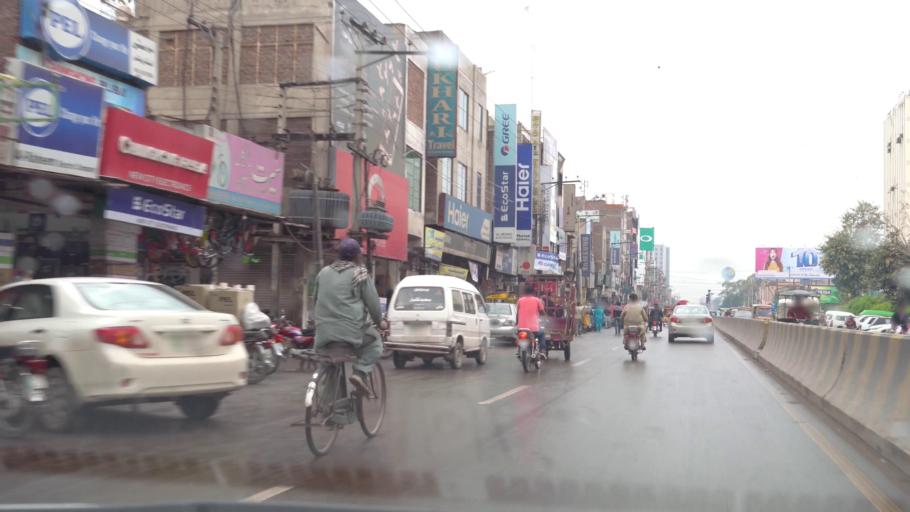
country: PK
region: Punjab
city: Faisalabad
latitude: 31.4174
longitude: 73.0869
